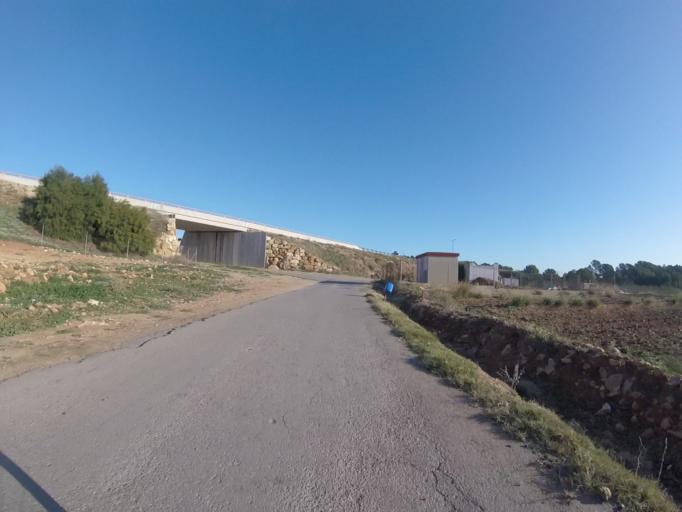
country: ES
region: Valencia
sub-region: Provincia de Castello
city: Torreblanca
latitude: 40.2309
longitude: 0.2023
